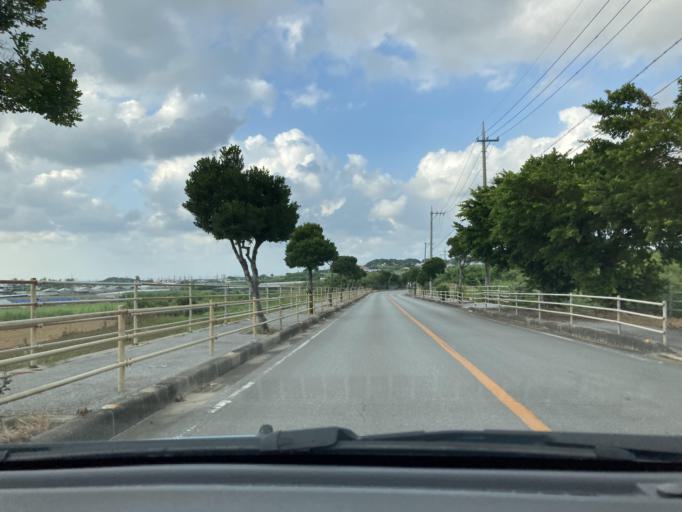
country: JP
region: Okinawa
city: Itoman
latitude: 26.0974
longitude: 127.6656
